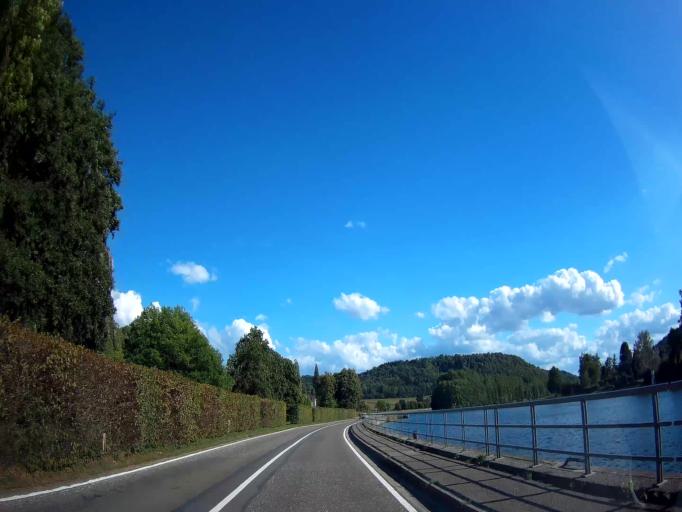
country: BE
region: Wallonia
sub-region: Province de Namur
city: Anhee
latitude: 50.3048
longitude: 4.8950
